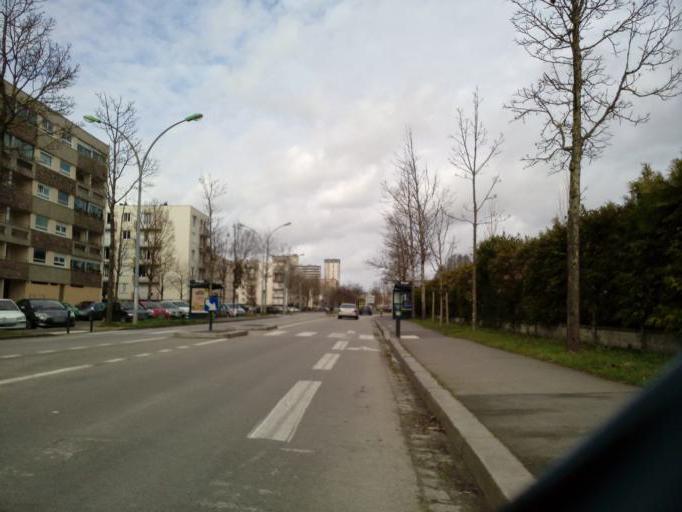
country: FR
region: Brittany
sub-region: Departement d'Ille-et-Vilaine
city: Rennes
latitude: 48.1159
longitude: -1.7048
